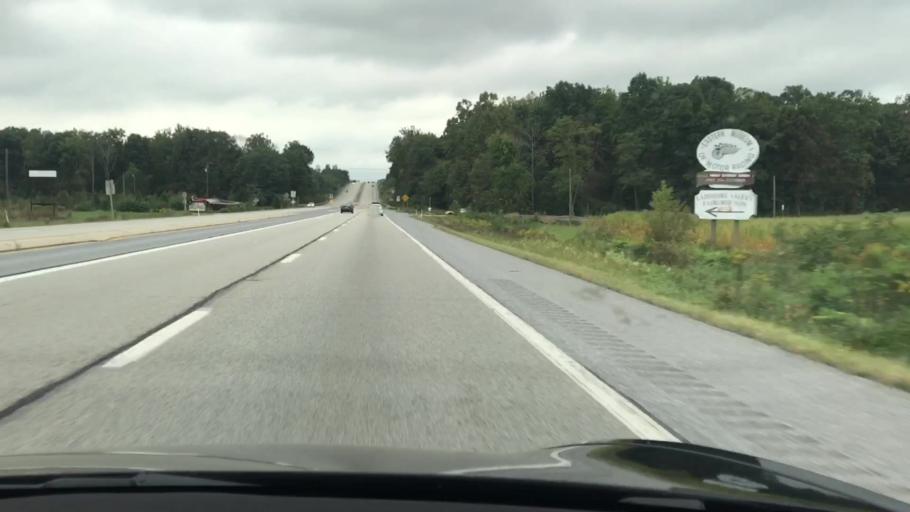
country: US
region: Pennsylvania
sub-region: Adams County
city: Lake Meade
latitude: 40.0293
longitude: -77.0845
